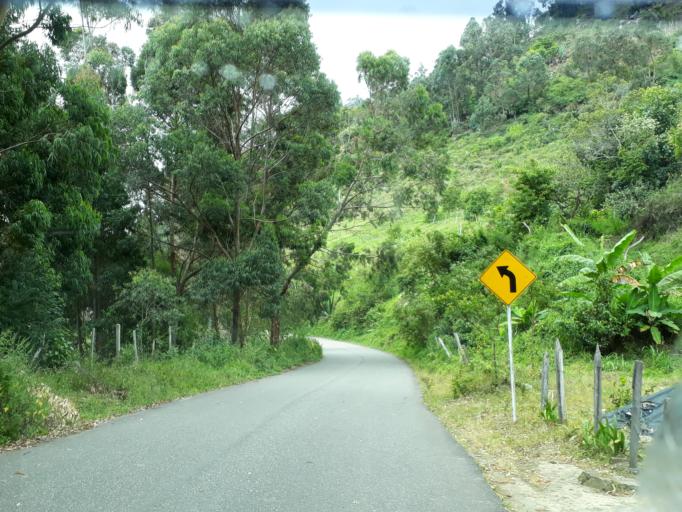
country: CO
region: Cundinamarca
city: Cabrera
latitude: 4.0186
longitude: -74.5116
